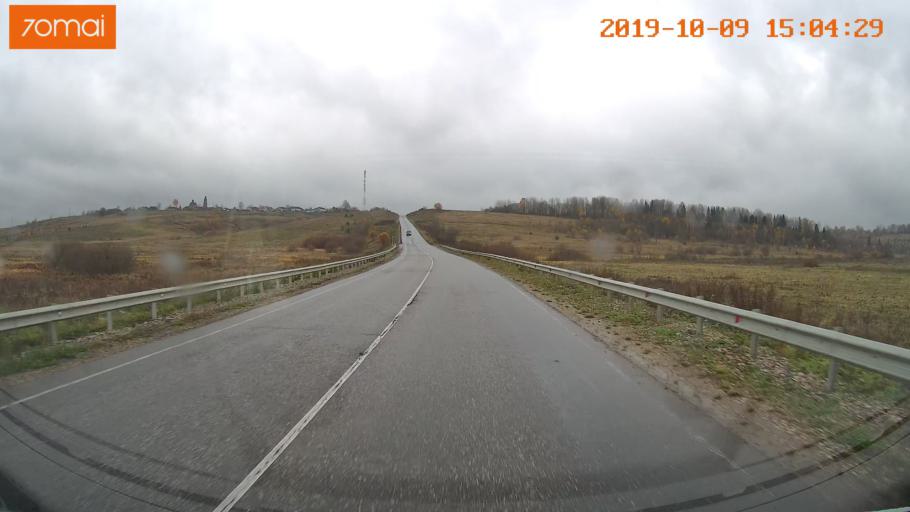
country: RU
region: Kostroma
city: Chistyye Bory
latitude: 58.2579
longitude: 41.6667
